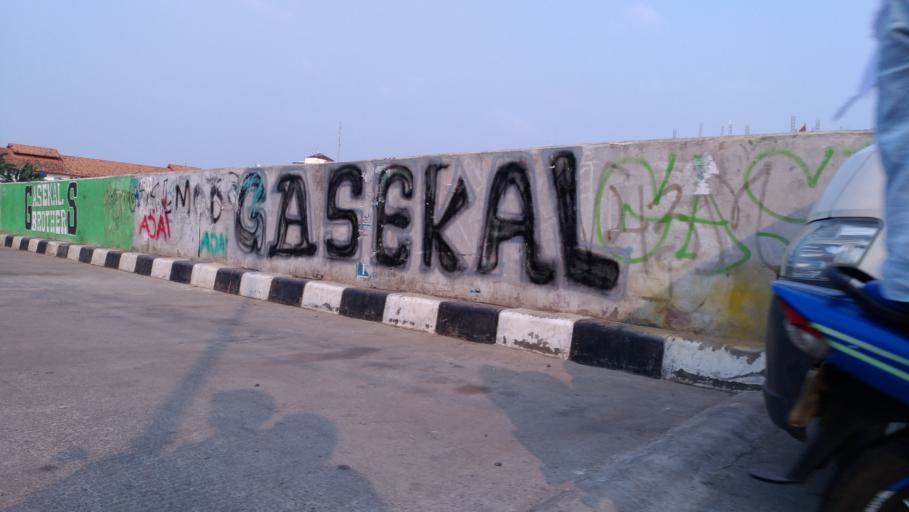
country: ID
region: Jakarta Raya
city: Jakarta
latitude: -6.2196
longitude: 106.8620
